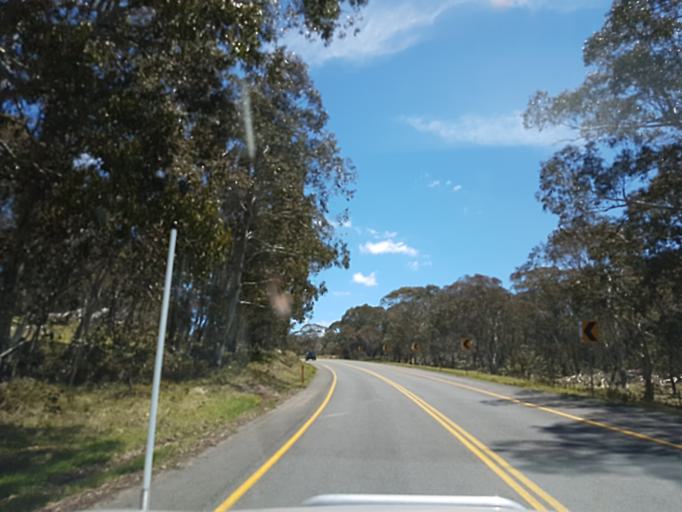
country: AU
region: Victoria
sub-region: Alpine
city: Mount Beauty
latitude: -37.0373
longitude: 147.3062
